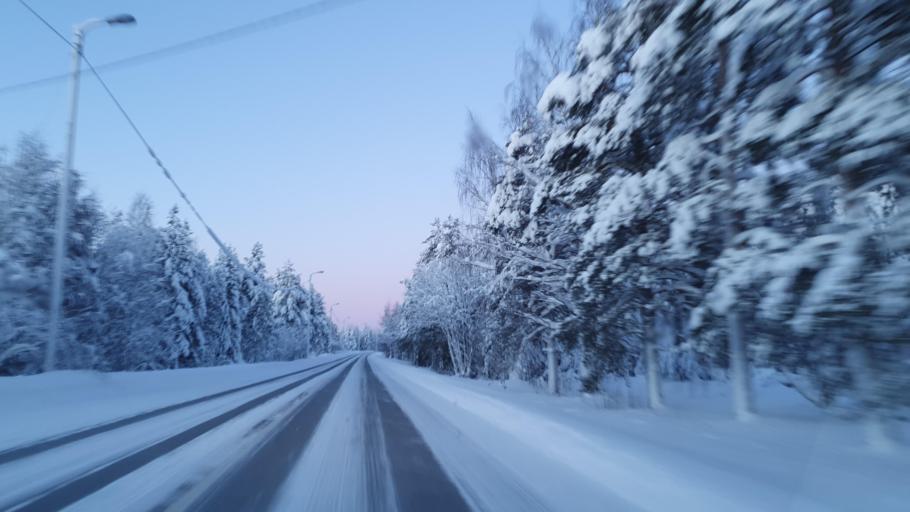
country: FI
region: Lapland
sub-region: Torniolaakso
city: Ylitornio
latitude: 66.1988
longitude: 23.7977
